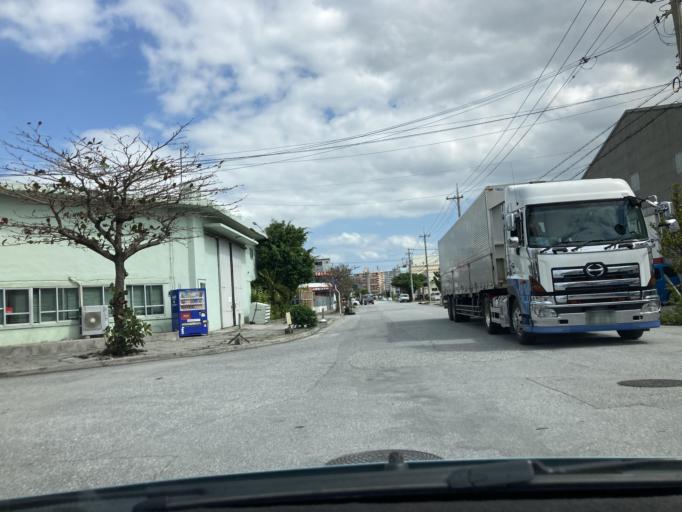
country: JP
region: Okinawa
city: Naha-shi
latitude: 26.2427
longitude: 127.6744
